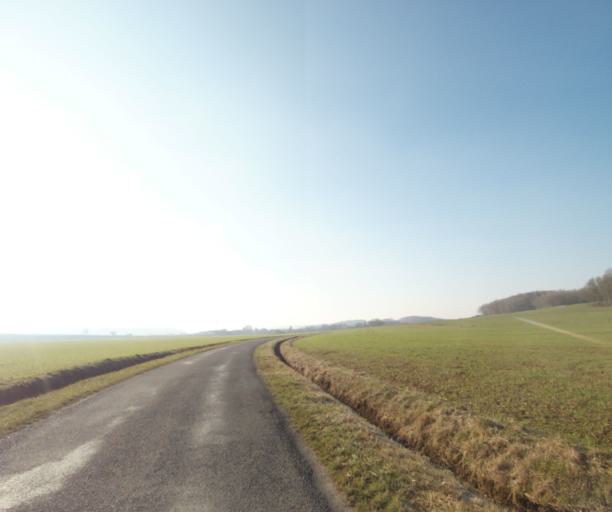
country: FR
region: Champagne-Ardenne
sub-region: Departement de la Haute-Marne
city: Bienville
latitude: 48.5459
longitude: 5.0330
